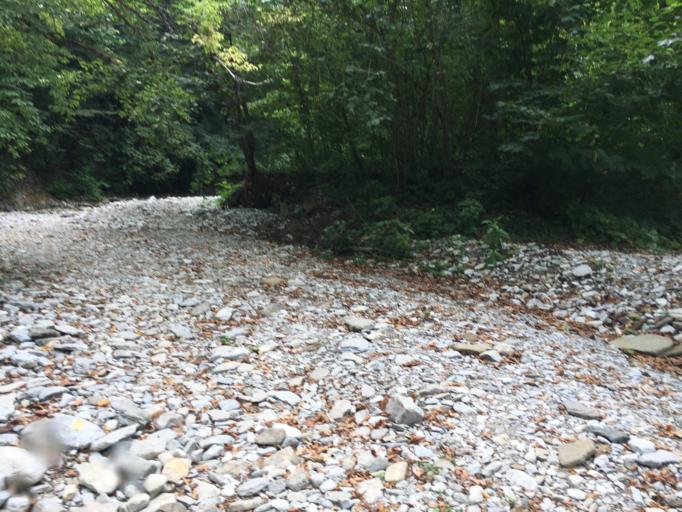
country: RU
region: Krasnodarskiy
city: Tuapse
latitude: 44.2566
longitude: 39.2194
